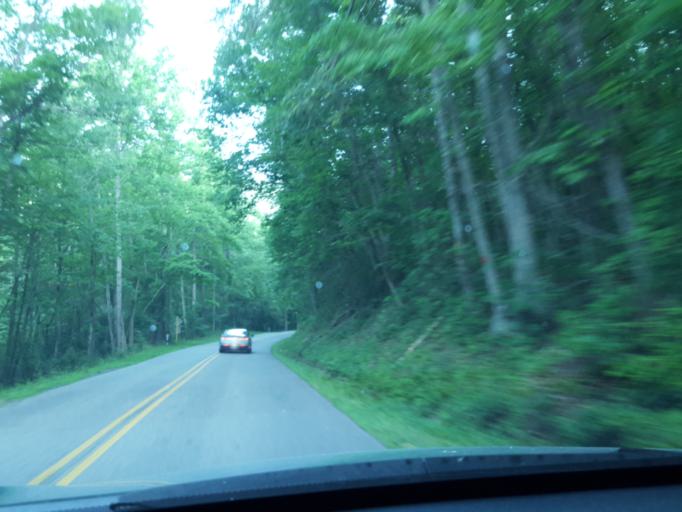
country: US
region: Virginia
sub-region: Augusta County
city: Lyndhurst
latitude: 37.9502
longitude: -78.9621
